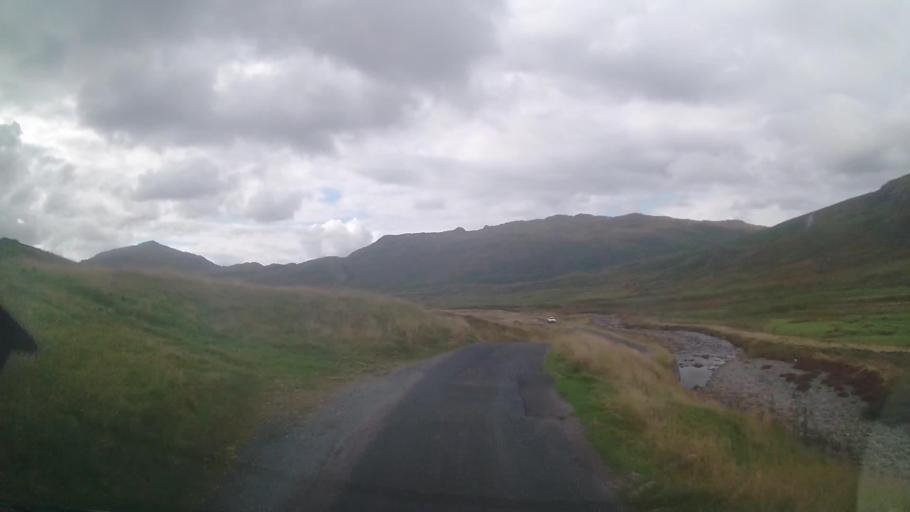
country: GB
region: England
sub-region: Cumbria
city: Ambleside
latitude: 54.4070
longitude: -3.1531
